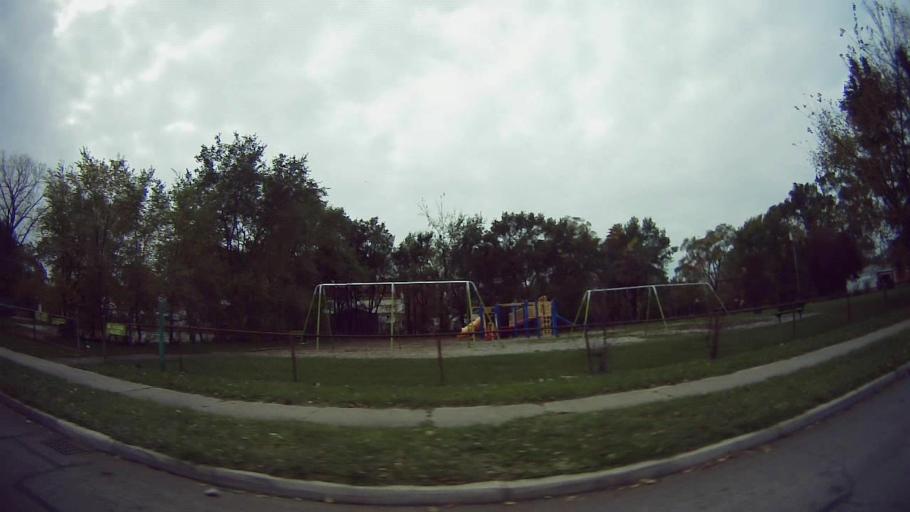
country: US
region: Michigan
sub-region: Wayne County
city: Highland Park
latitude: 42.4287
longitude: -83.0827
